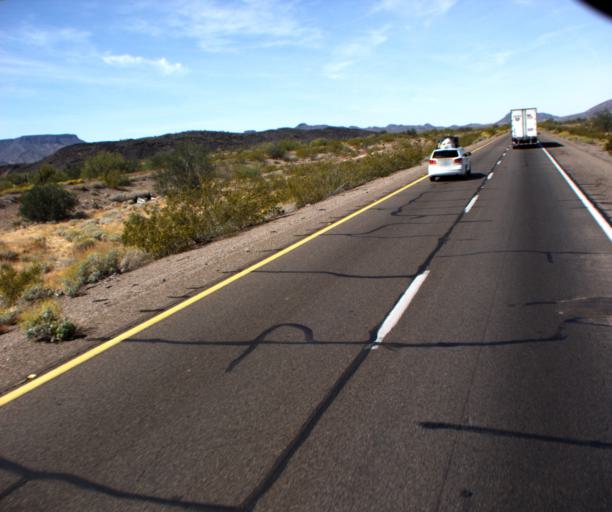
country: US
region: Arizona
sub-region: La Paz County
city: Quartzsite
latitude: 33.6529
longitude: -113.9348
